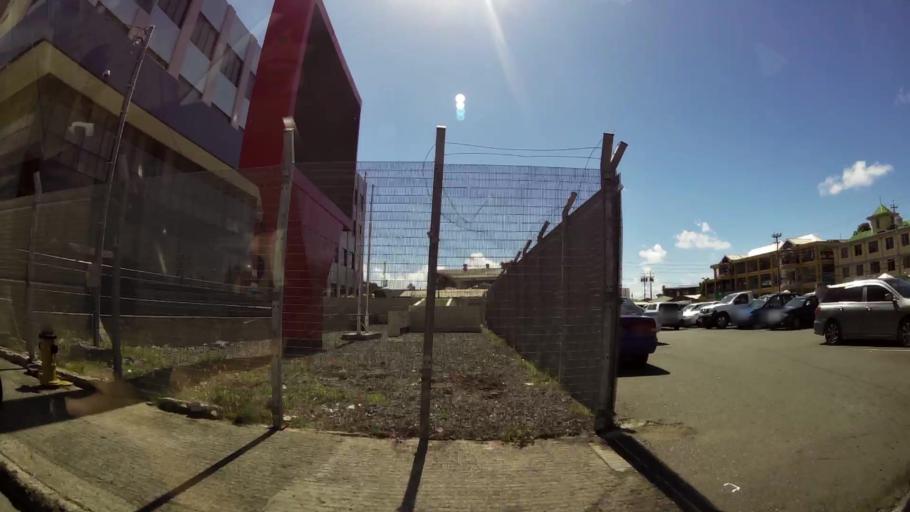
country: TT
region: Tobago
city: Scarborough
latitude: 11.1847
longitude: -60.7376
